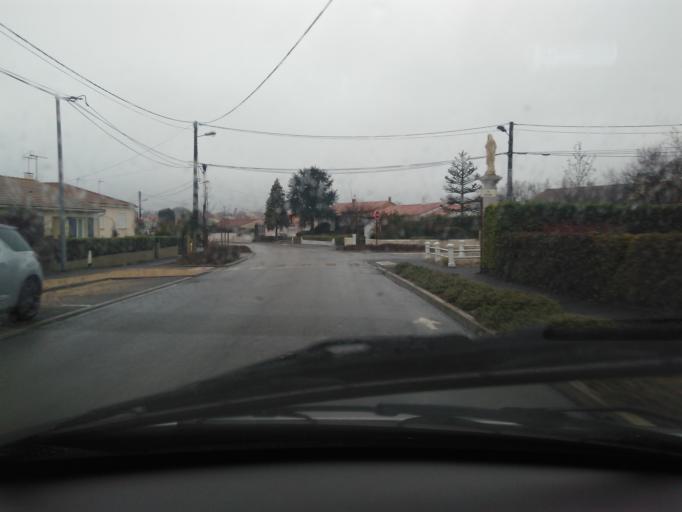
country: FR
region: Pays de la Loire
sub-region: Departement de la Vendee
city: La Ferriere
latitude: 46.7089
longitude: -1.3108
